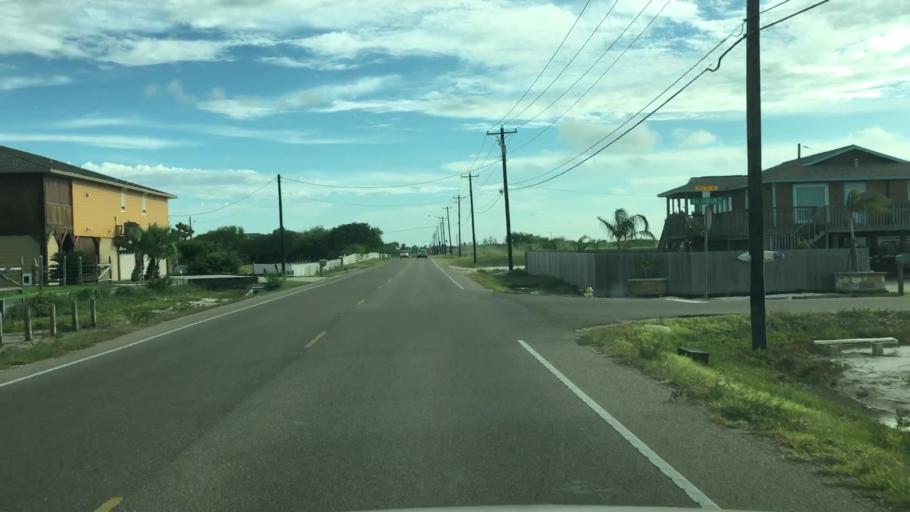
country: US
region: Texas
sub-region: Nueces County
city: Corpus Christi
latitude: 27.6477
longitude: -97.2821
